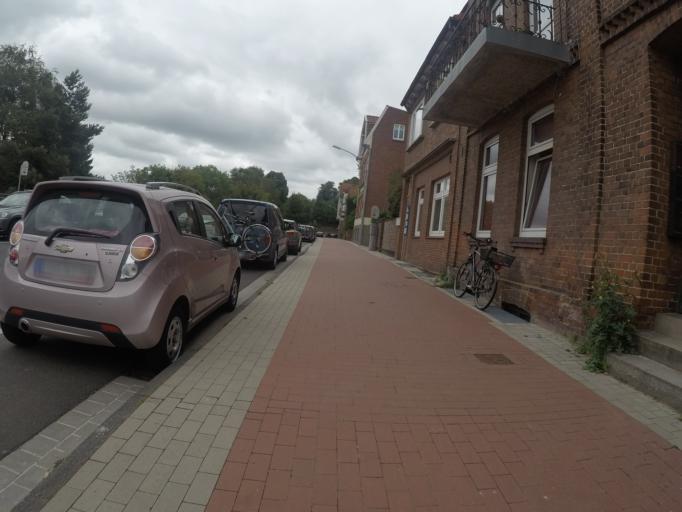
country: DE
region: Lower Saxony
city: Stade
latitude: 53.6002
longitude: 9.4794
